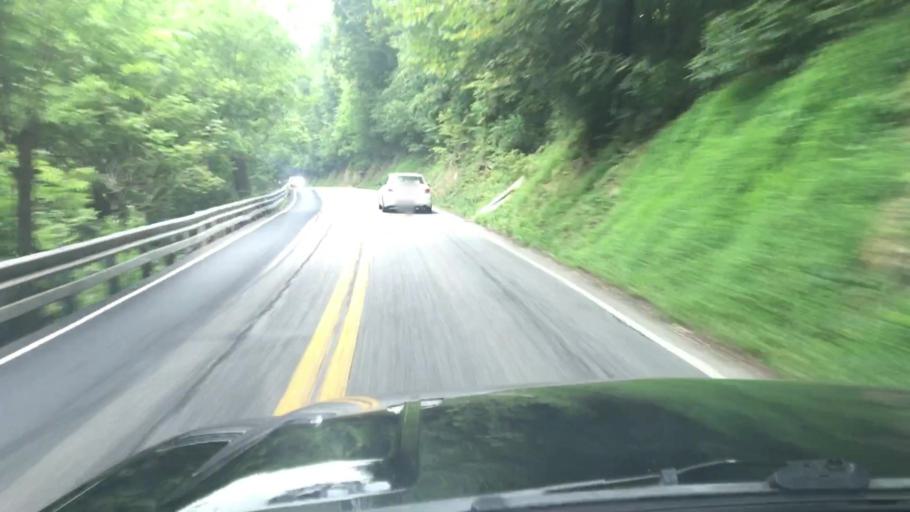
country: US
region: Pennsylvania
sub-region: Cumberland County
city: Shiremanstown
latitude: 40.2526
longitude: -76.9743
